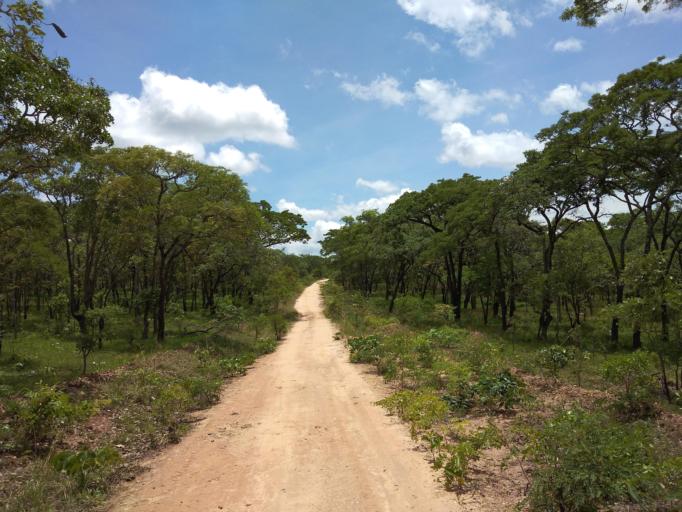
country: ZM
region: Central
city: Mkushi
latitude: -13.9282
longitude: 29.8640
